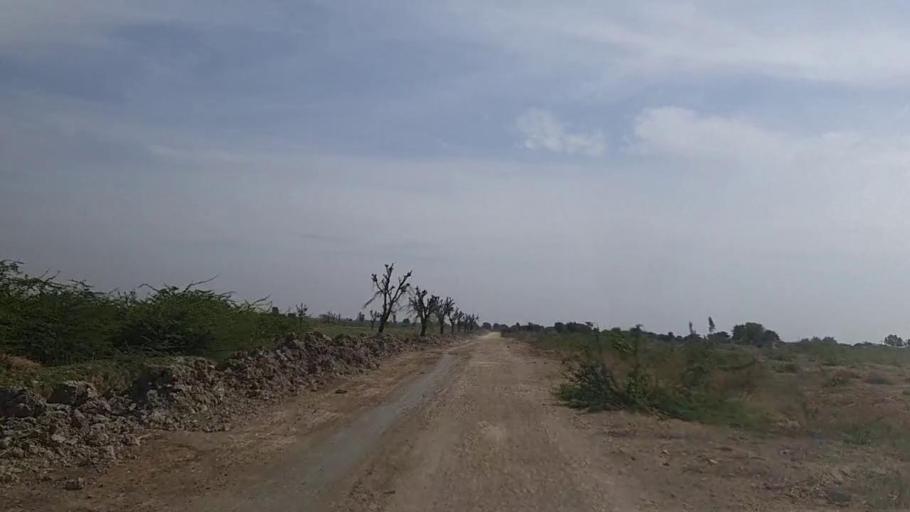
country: PK
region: Sindh
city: Samaro
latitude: 25.2031
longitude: 69.4624
